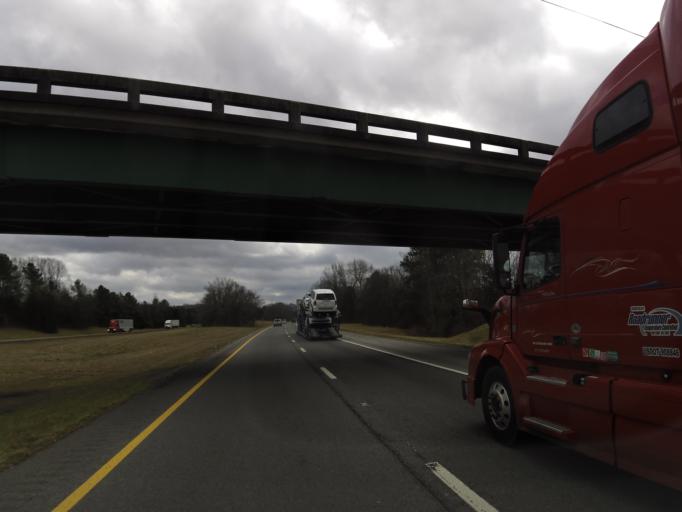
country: US
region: Tennessee
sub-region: Rutherford County
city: Plainview
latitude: 35.6192
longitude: -86.2414
